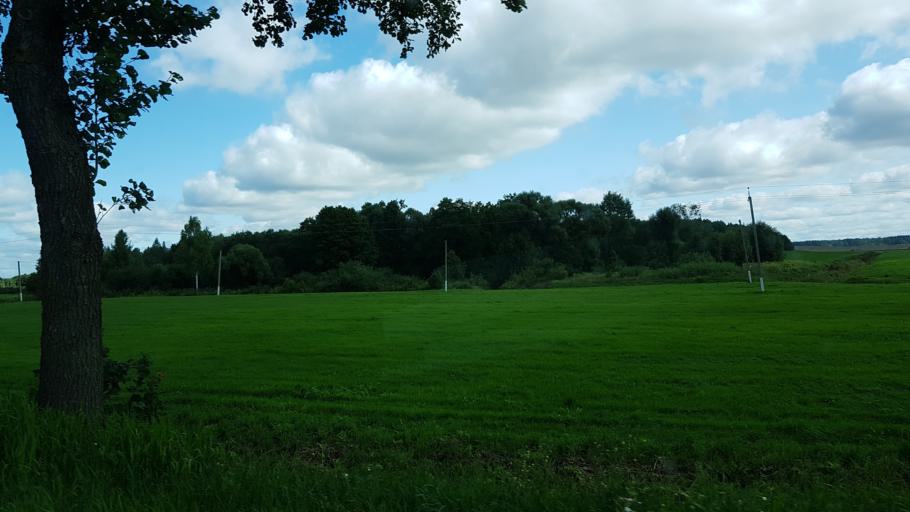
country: BY
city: Fanipol
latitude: 53.7682
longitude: 27.3256
